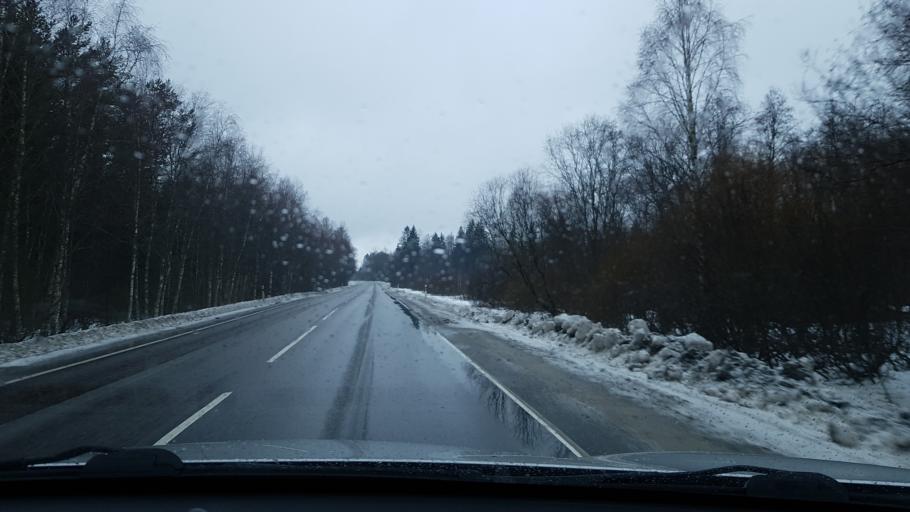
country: EE
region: Raplamaa
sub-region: Kehtna vald
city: Kehtna
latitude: 58.8801
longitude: 24.9819
